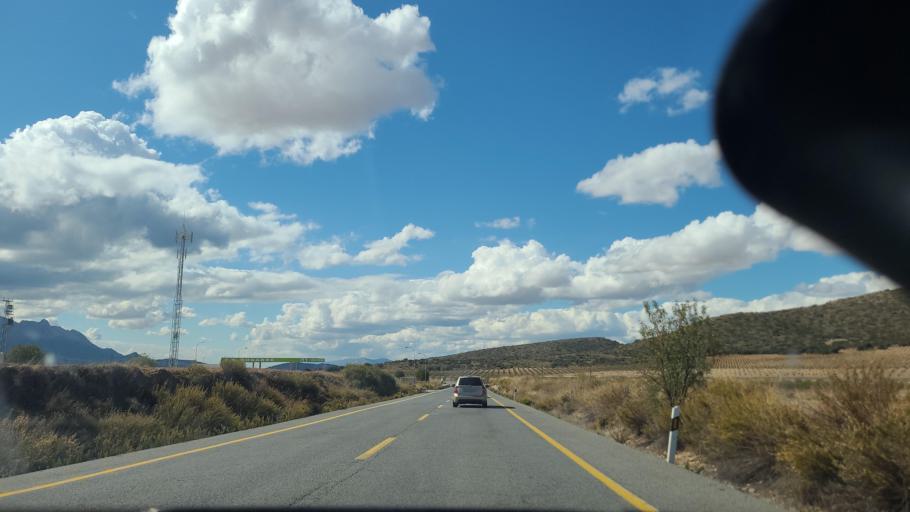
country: ES
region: Andalusia
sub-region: Provincia de Granada
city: Pinar
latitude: 37.4059
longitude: -3.3869
